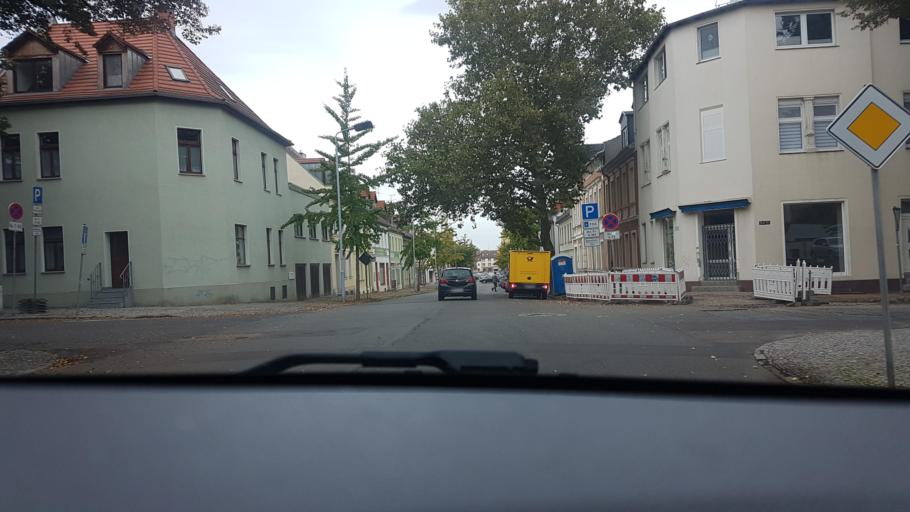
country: DE
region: Saxony-Anhalt
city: Bernburg
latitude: 51.7922
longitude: 11.7471
